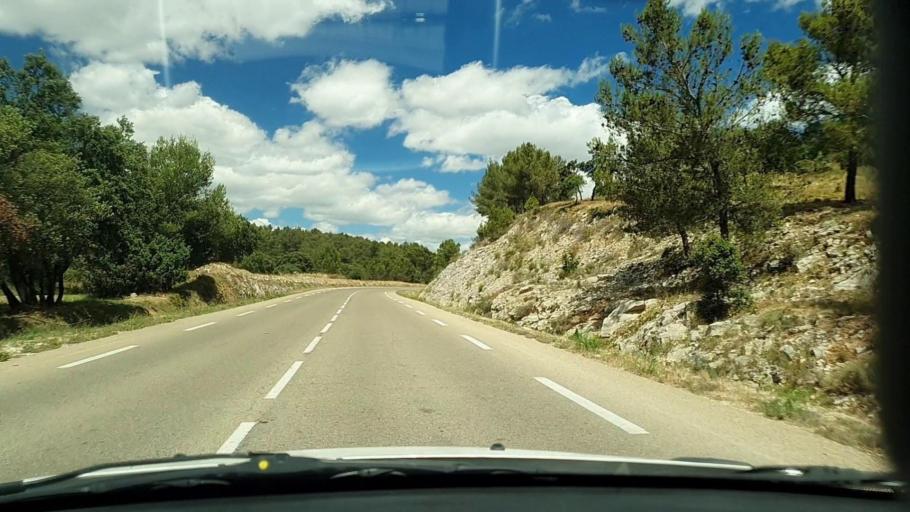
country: FR
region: Languedoc-Roussillon
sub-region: Departement du Gard
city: Poulx
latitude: 43.8876
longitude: 4.4173
